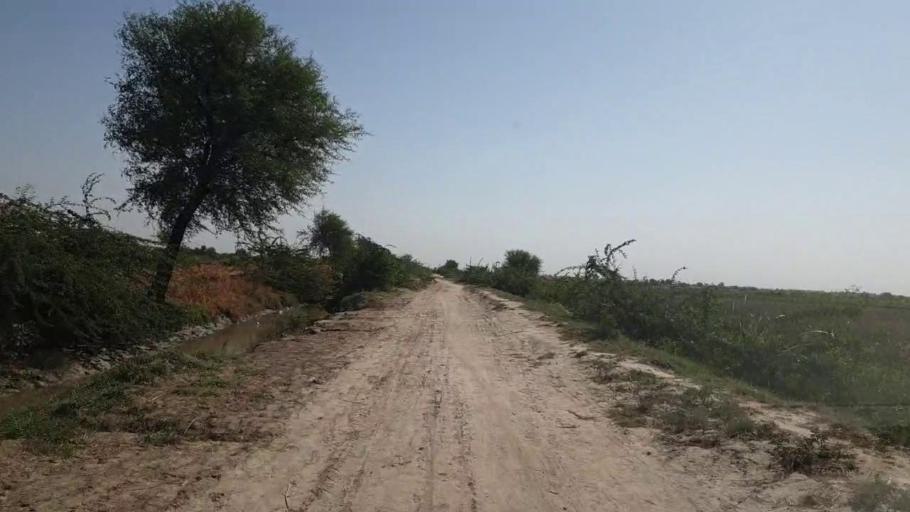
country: PK
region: Sindh
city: Kadhan
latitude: 24.6142
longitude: 68.9981
